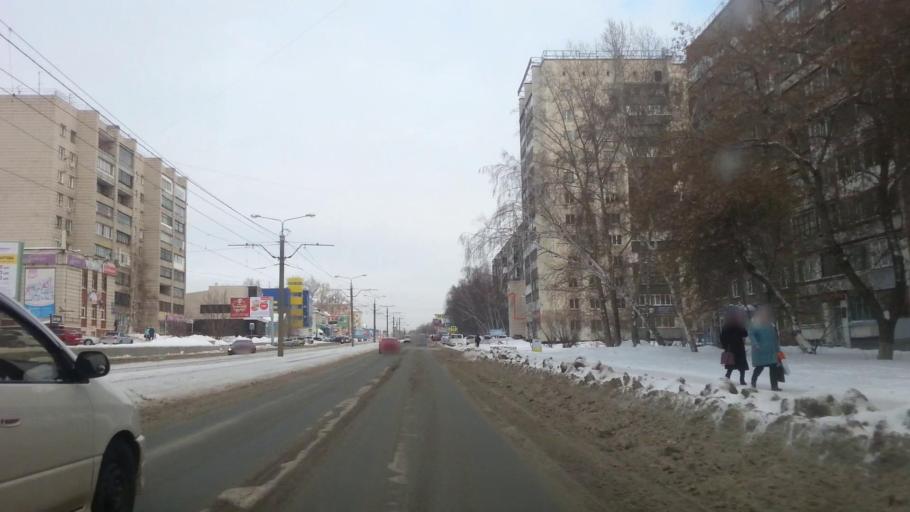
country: RU
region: Altai Krai
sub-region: Gorod Barnaulskiy
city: Barnaul
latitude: 53.3713
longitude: 83.7448
